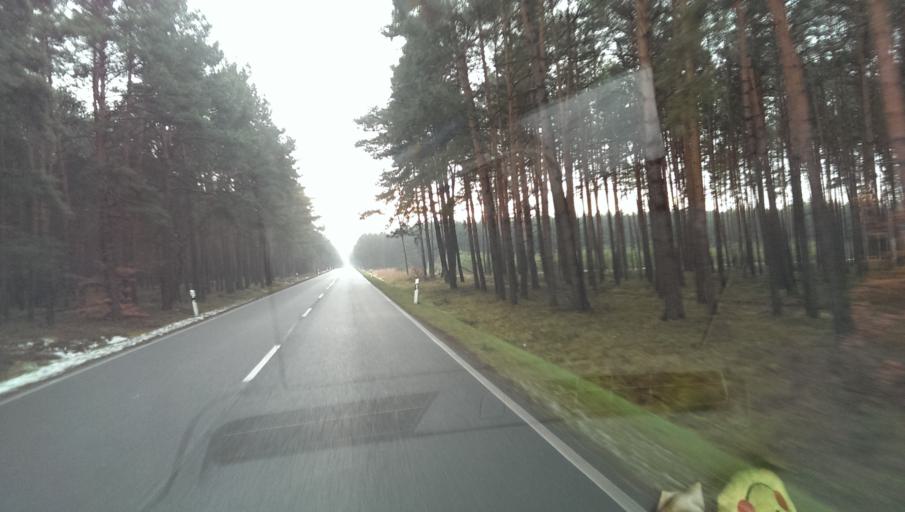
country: DE
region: Saxony-Anhalt
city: Holzdorf
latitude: 51.8687
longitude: 13.1450
